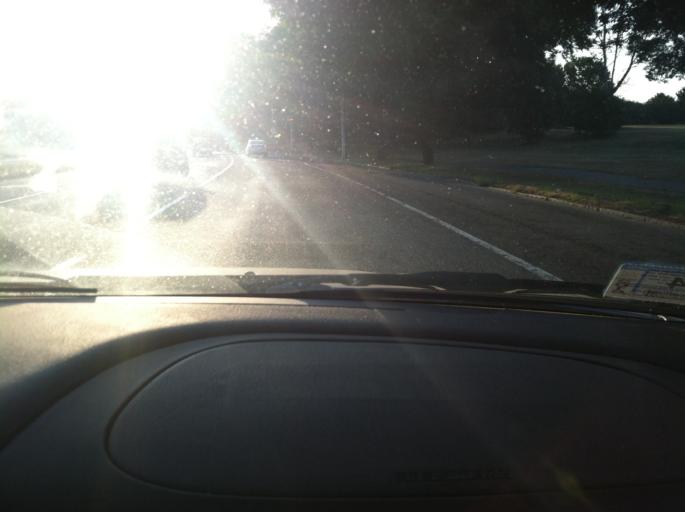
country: US
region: Massachusetts
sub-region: Middlesex County
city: Medford
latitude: 42.4106
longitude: -71.1038
